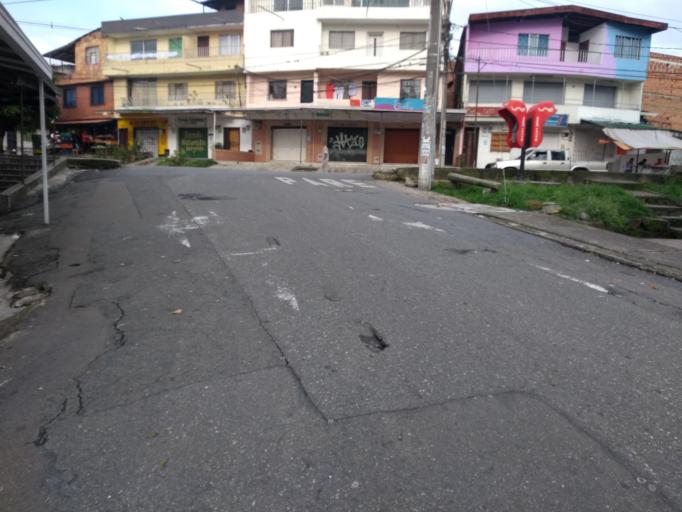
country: CO
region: Antioquia
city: Bello
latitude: 6.3035
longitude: -75.5704
